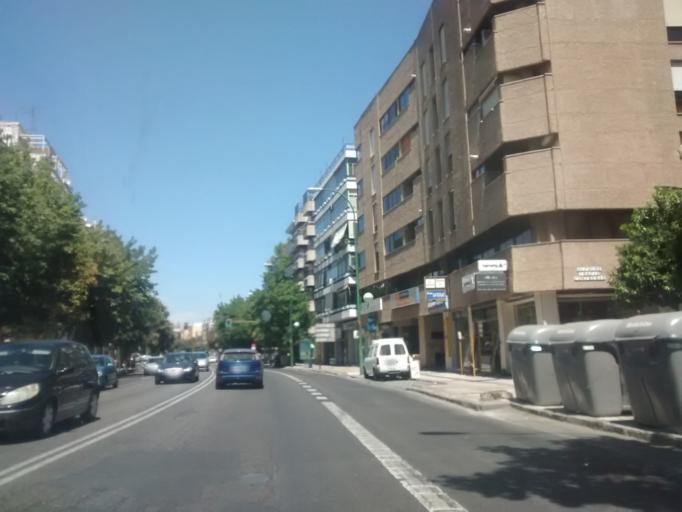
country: ES
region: Andalusia
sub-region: Provincia de Sevilla
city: Sevilla
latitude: 37.3869
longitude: -5.9853
